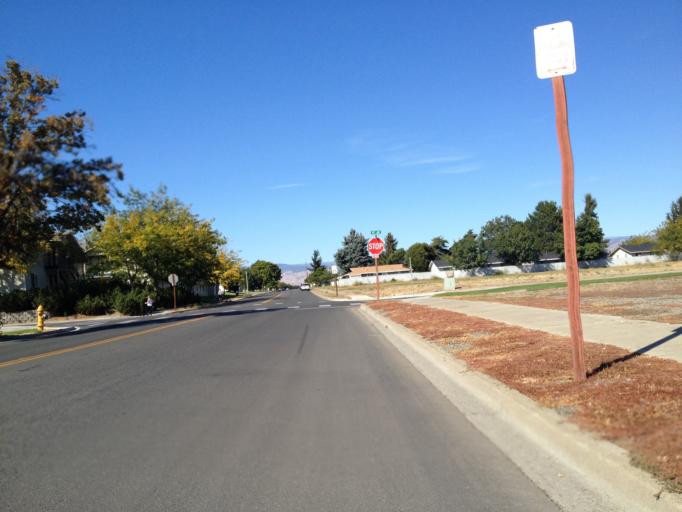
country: US
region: Washington
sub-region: Kittitas County
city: Ellensburg
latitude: 47.0100
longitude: -120.5317
